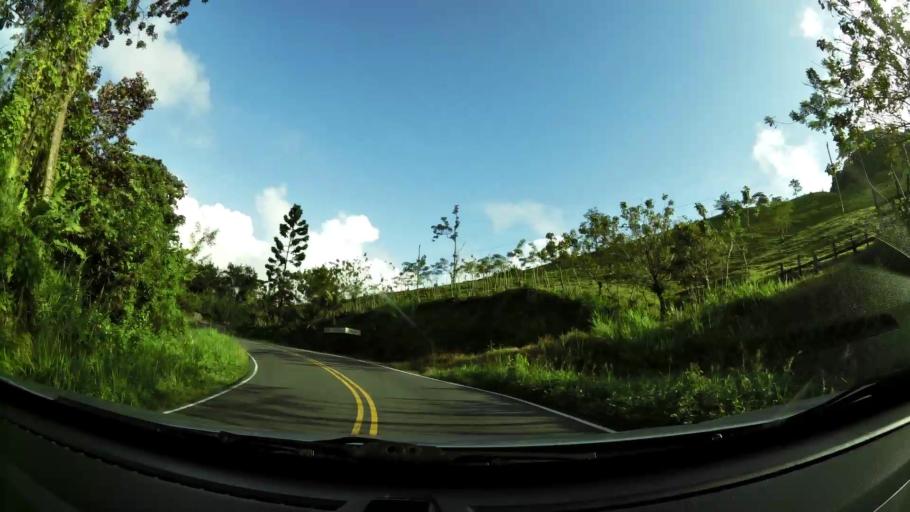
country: CR
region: Limon
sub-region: Canton de Siquirres
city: Siquirres
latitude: 10.0548
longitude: -83.5524
